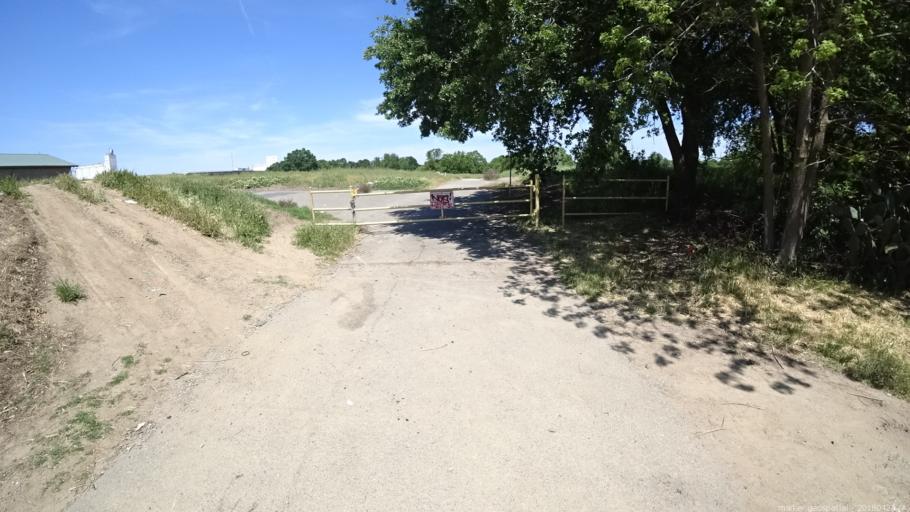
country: US
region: California
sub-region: Yolo County
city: West Sacramento
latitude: 38.5593
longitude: -121.5377
